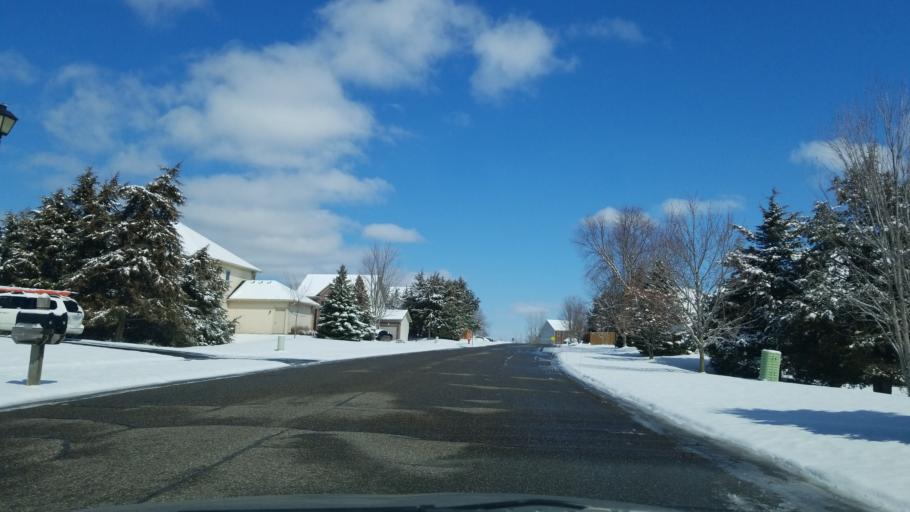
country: US
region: Wisconsin
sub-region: Saint Croix County
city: Hudson
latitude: 44.9549
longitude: -92.7022
